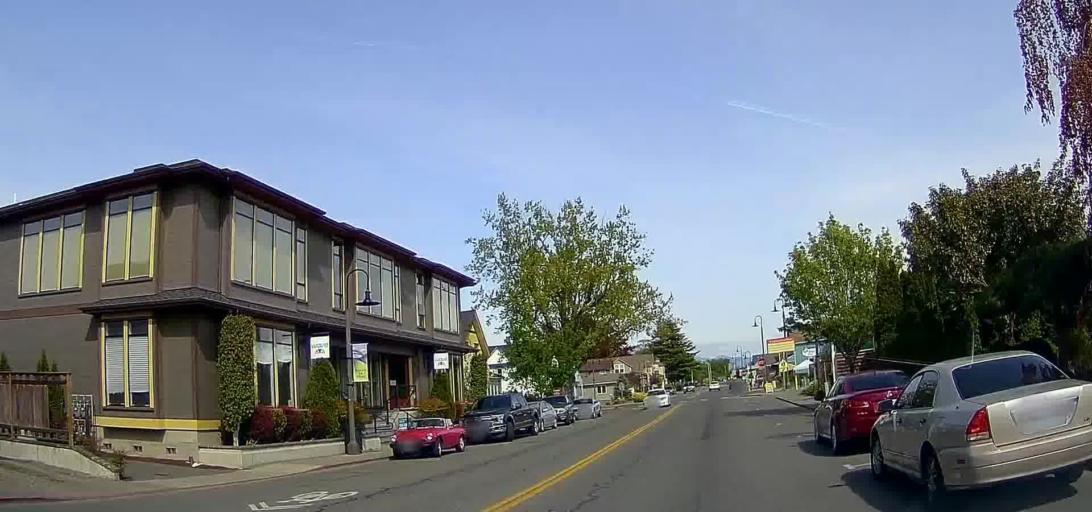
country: US
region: Washington
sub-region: Skagit County
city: Mount Vernon
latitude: 48.3920
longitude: -122.4910
